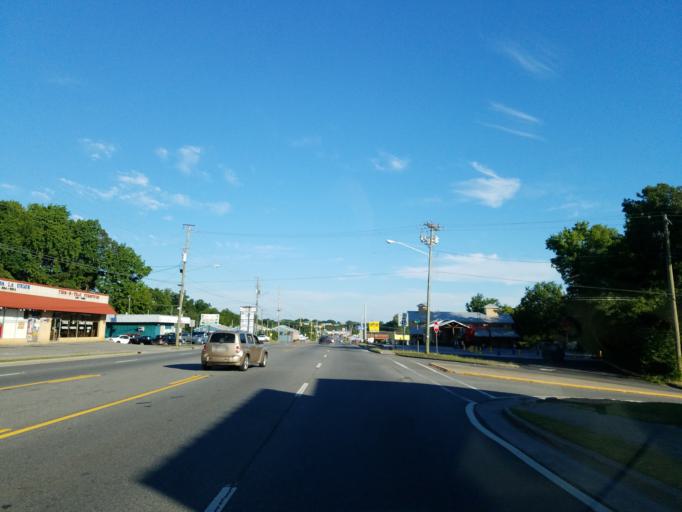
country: US
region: Georgia
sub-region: Gordon County
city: Calhoun
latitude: 34.4919
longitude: -84.9489
